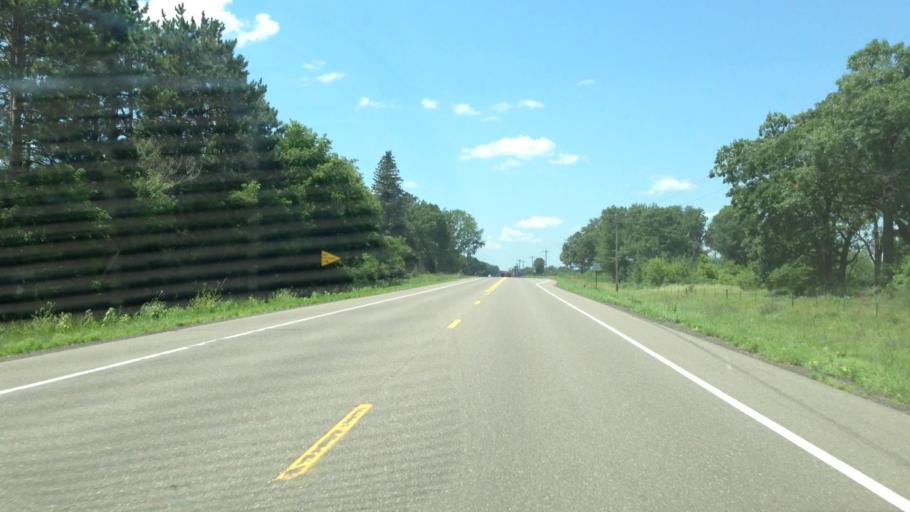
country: US
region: Minnesota
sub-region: Sherburne County
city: Zimmerman
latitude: 45.4439
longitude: -93.6712
